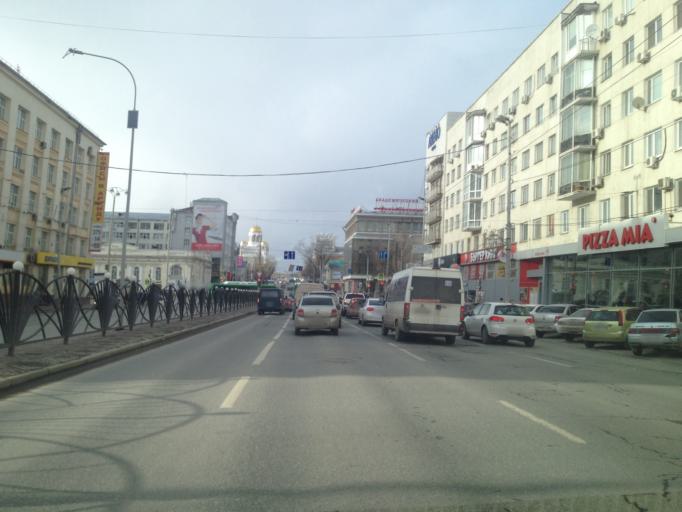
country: RU
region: Sverdlovsk
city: Yekaterinburg
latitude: 56.8381
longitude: 60.6119
